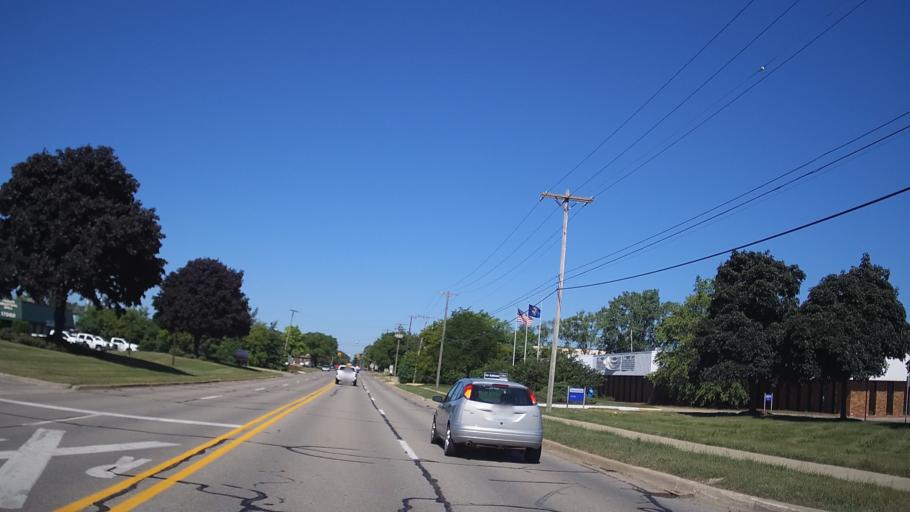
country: US
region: Michigan
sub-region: Macomb County
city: Fraser
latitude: 42.5316
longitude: -82.9443
